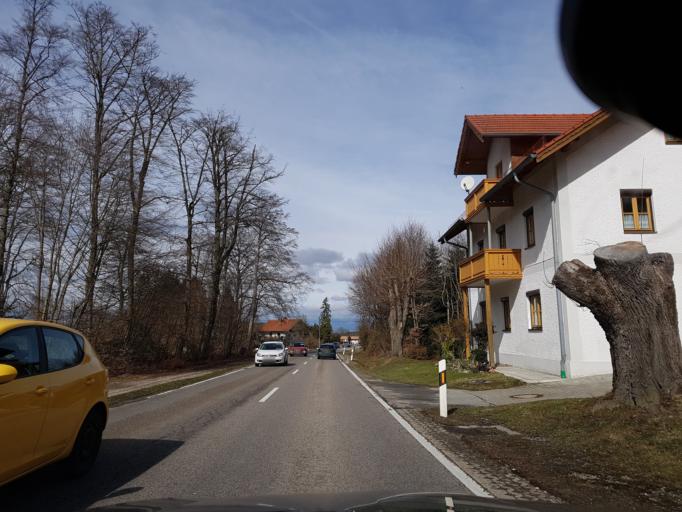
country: DE
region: Bavaria
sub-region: Upper Bavaria
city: Aying
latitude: 47.9363
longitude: 11.7987
